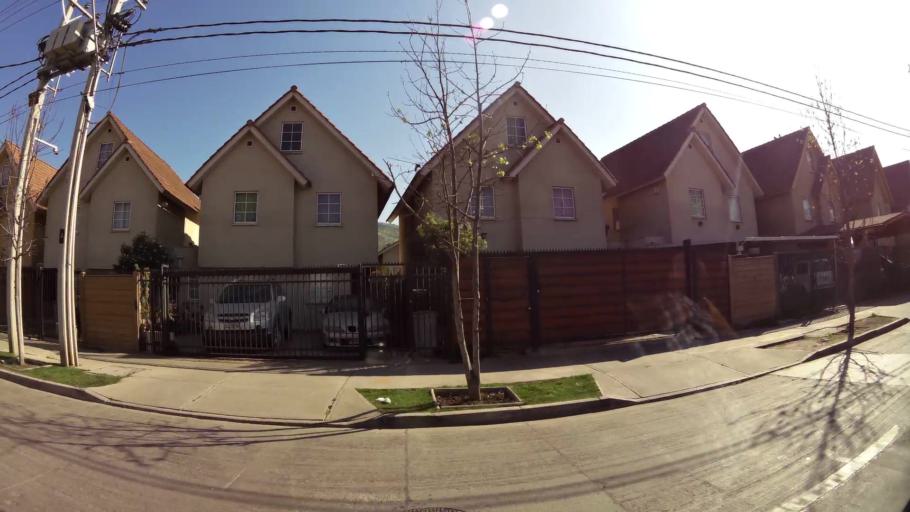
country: CL
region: Santiago Metropolitan
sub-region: Provincia de Chacabuco
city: Chicureo Abajo
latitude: -33.3540
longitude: -70.6850
